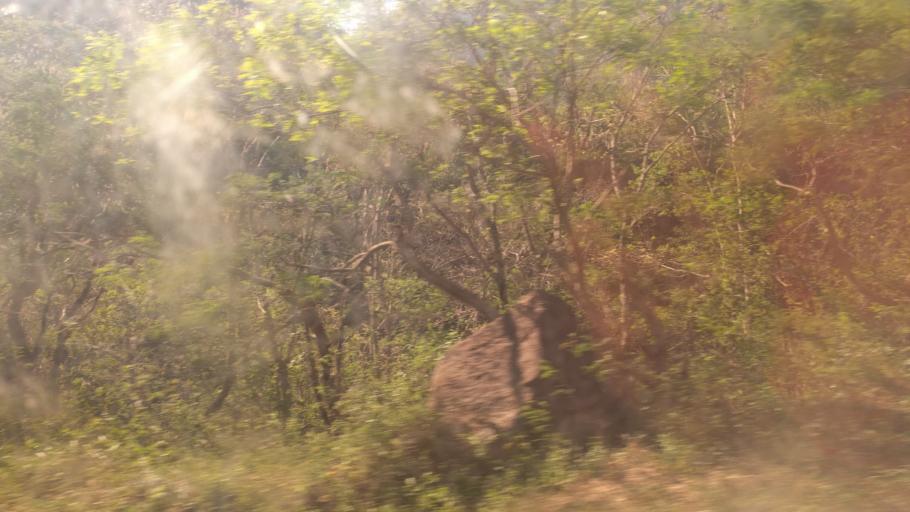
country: BO
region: Santa Cruz
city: Jorochito
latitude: -18.1691
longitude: -63.5795
